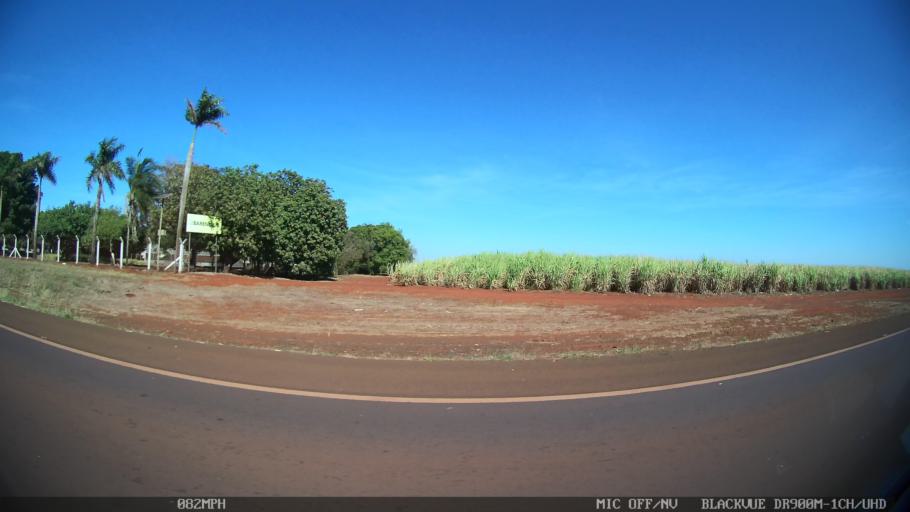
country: BR
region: Sao Paulo
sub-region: Guaira
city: Guaira
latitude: -20.4441
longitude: -48.2922
